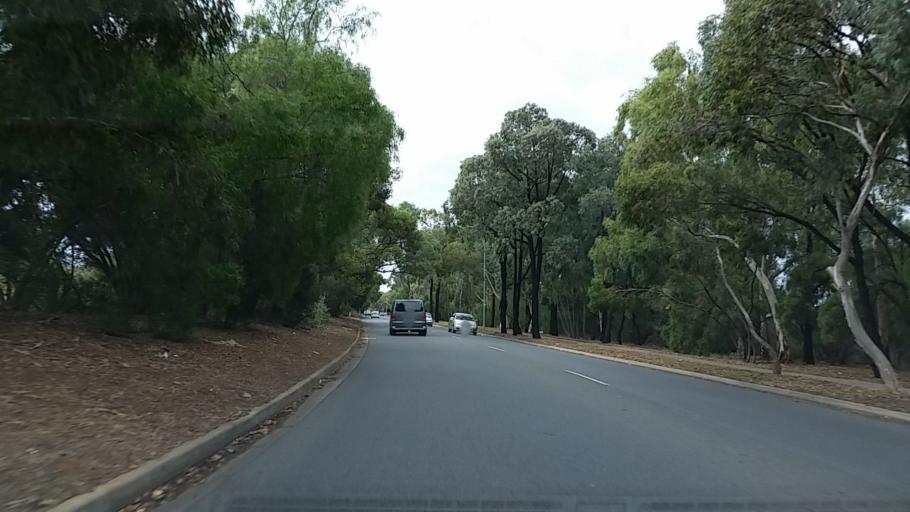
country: AU
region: South Australia
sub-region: Salisbury
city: Salisbury
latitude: -34.7806
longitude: 138.6095
